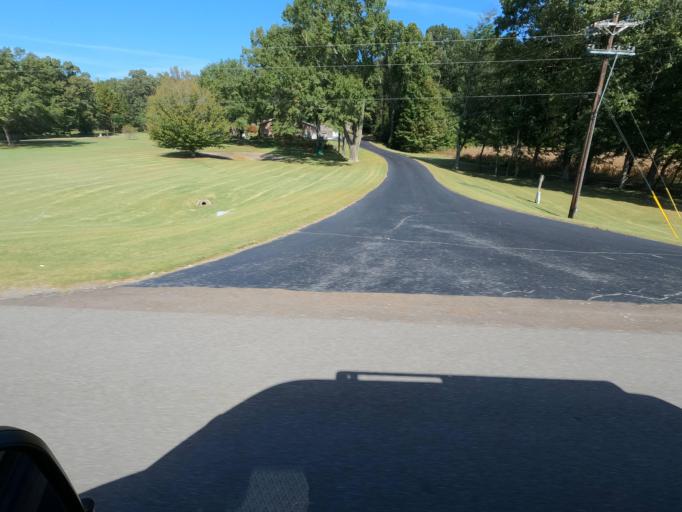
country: US
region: Tennessee
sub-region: Madison County
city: Three Way
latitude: 35.6697
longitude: -88.9300
